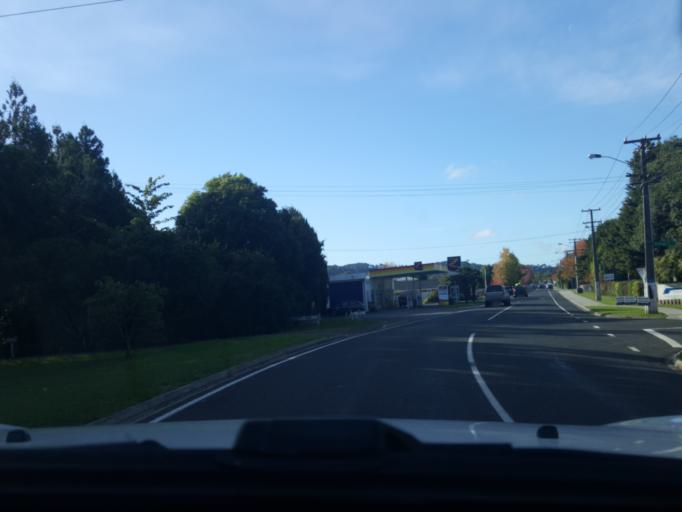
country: NZ
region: Auckland
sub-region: Auckland
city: Rosebank
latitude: -36.7621
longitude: 174.5878
